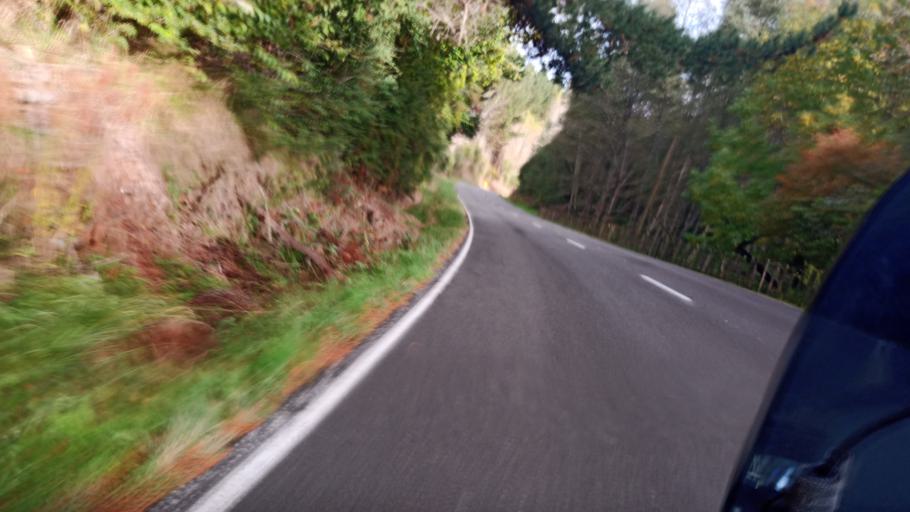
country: NZ
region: Gisborne
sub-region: Gisborne District
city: Gisborne
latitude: -38.5623
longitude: 177.7133
